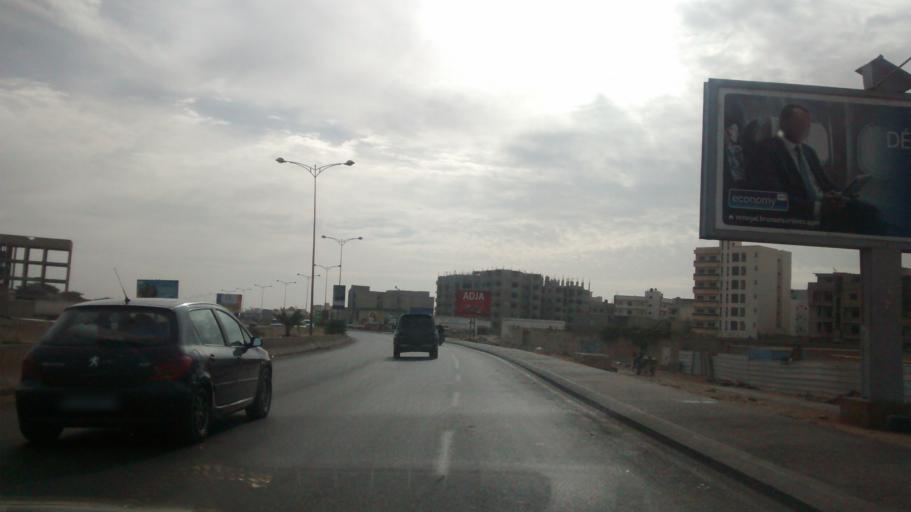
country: SN
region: Dakar
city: Grand Dakar
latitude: 14.7465
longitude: -17.4611
